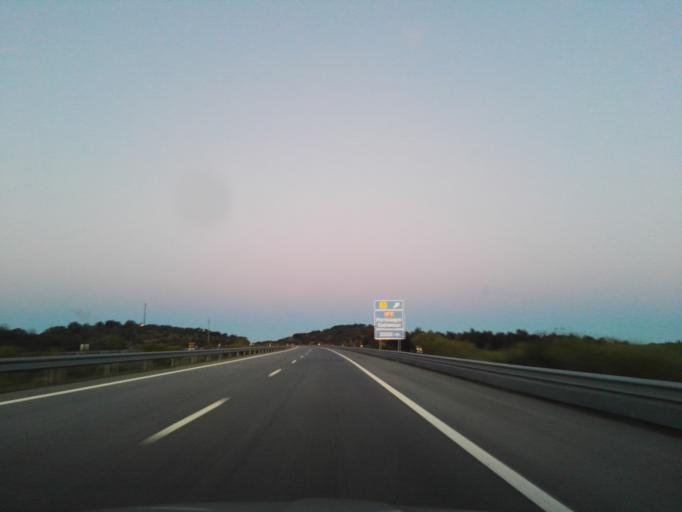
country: PT
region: Evora
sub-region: Estremoz
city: Estremoz
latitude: 38.8080
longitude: -7.6298
